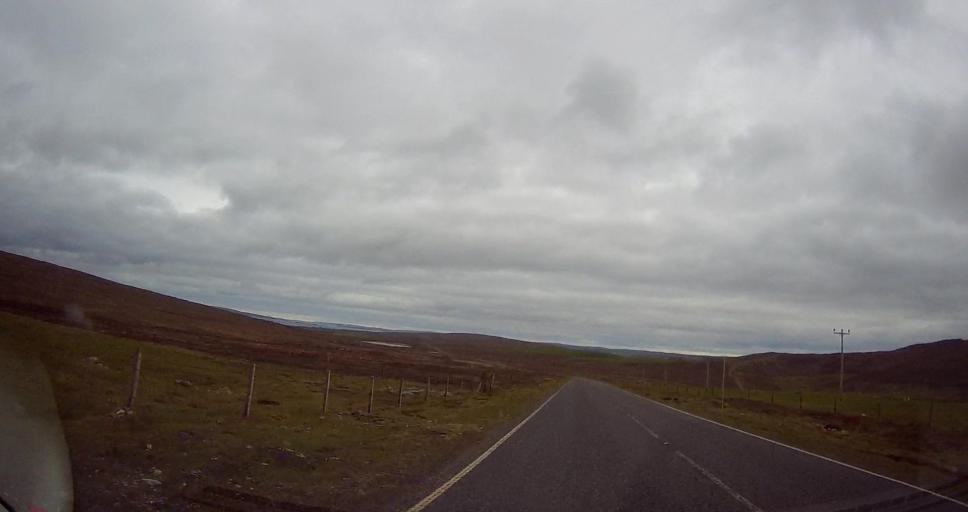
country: GB
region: Scotland
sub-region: Shetland Islands
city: Shetland
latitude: 60.7262
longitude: -0.9036
